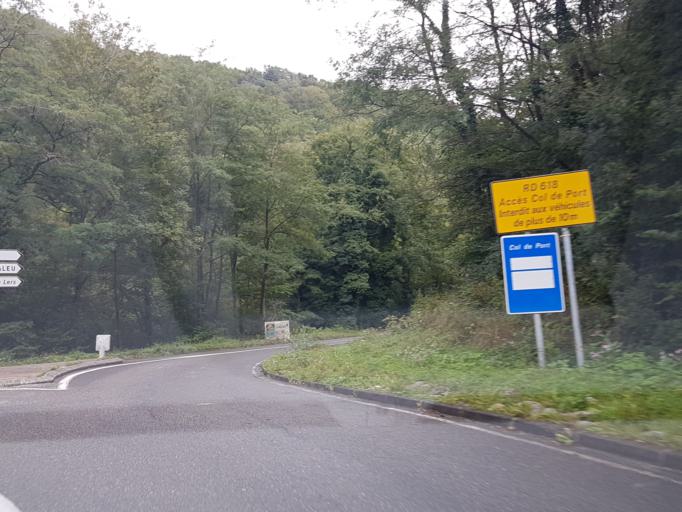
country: FR
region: Midi-Pyrenees
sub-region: Departement de l'Ariege
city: Saint-Girons
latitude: 42.9089
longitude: 1.2148
